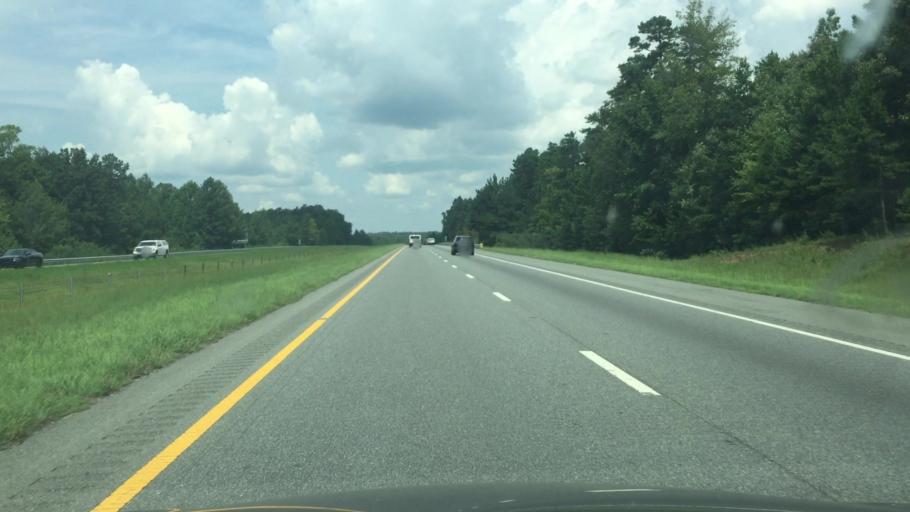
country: US
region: North Carolina
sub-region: Randolph County
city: Asheboro
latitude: 35.5511
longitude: -79.7983
